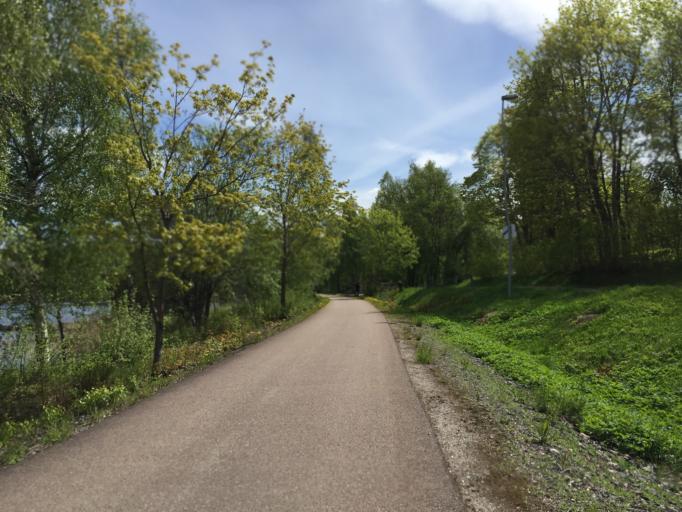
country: SE
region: Dalarna
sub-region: Ludvika Kommun
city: Ludvika
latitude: 60.1387
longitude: 15.1651
